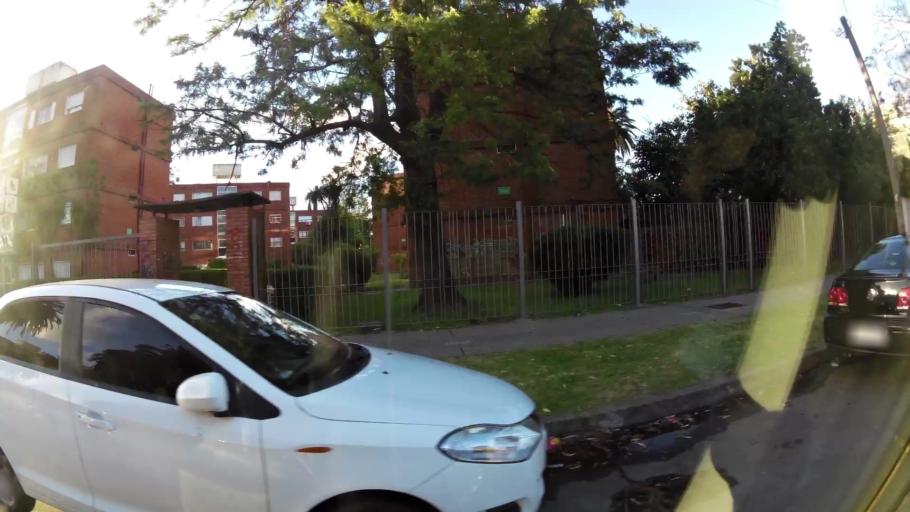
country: UY
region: Montevideo
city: Montevideo
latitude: -34.8818
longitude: -56.1495
